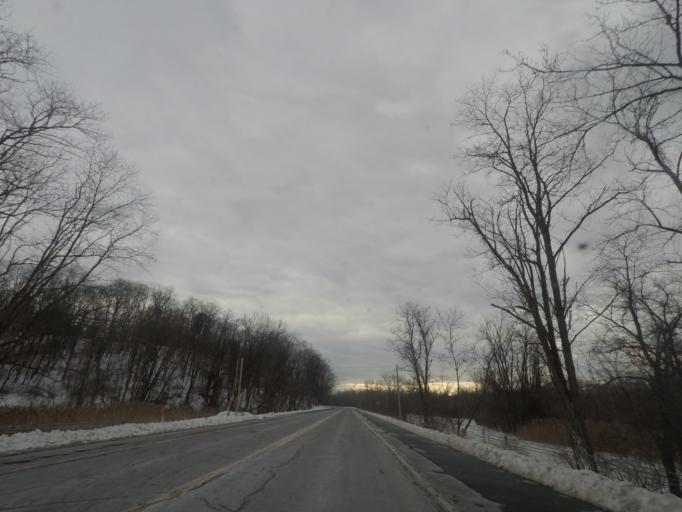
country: US
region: New York
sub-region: Rensselaer County
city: Castleton-on-Hudson
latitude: 42.5618
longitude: -73.7440
